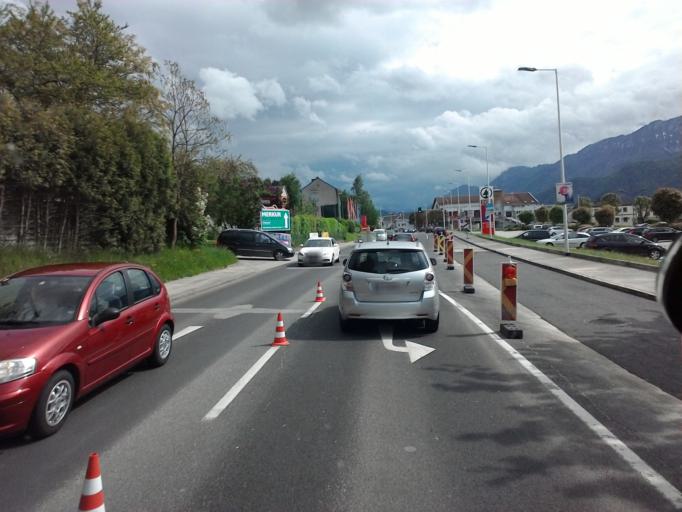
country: AT
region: Upper Austria
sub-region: Politischer Bezirk Kirchdorf an der Krems
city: Micheldorf in Oberoesterreich
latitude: 47.9079
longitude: 14.1190
